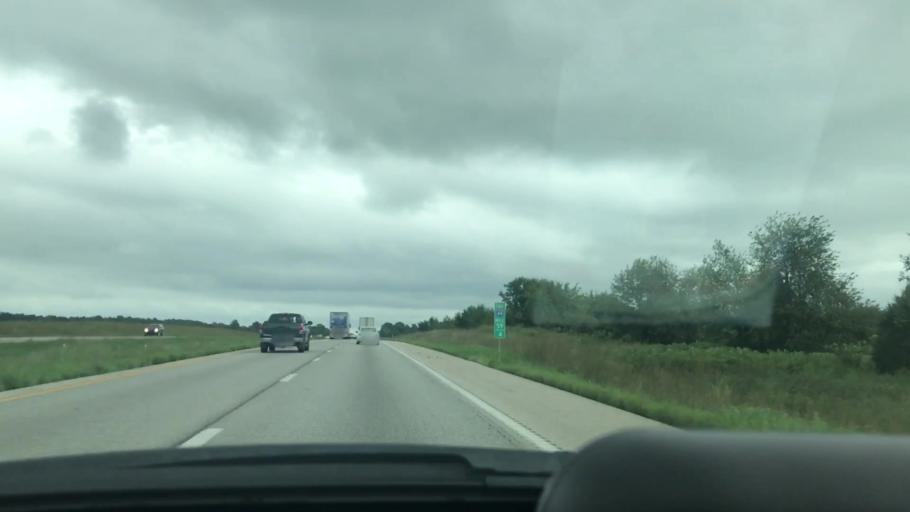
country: US
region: Missouri
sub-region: Greene County
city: Ash Grove
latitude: 37.1862
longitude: -93.6153
